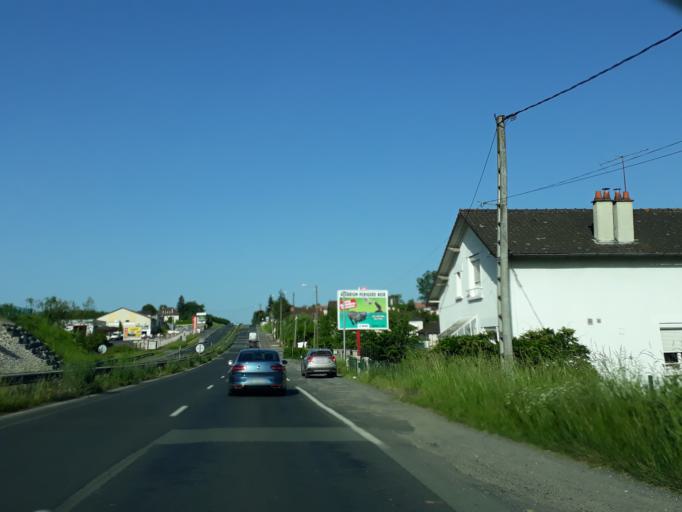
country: FR
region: Limousin
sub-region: Departement de la Correze
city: Saint-Pantaleon-de-Larche
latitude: 45.1426
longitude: 1.4683
